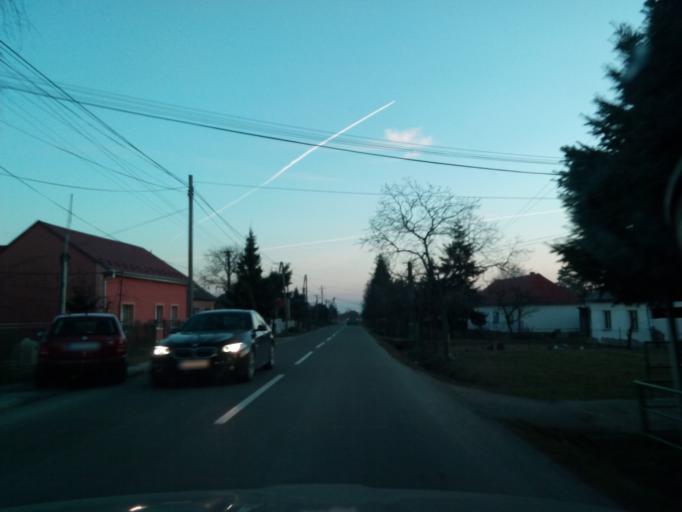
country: SK
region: Kosicky
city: Sobrance
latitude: 48.7862
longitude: 22.1320
